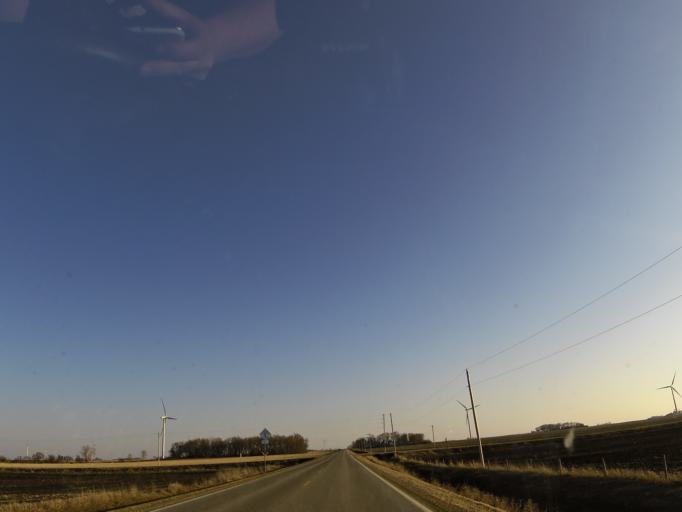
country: US
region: Iowa
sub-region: Worth County
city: Northwood
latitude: 43.4021
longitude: -93.1242
